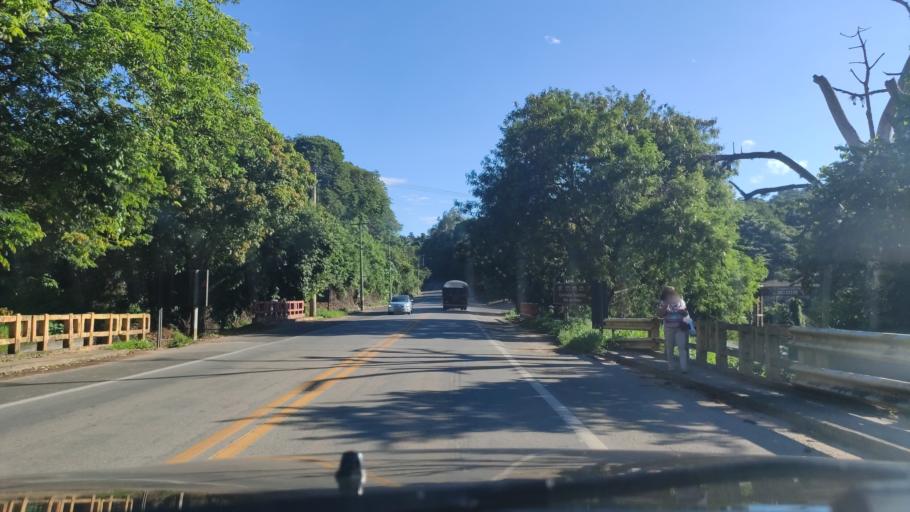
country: BR
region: Sao Paulo
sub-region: Socorro
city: Socorro
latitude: -22.5963
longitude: -46.5173
